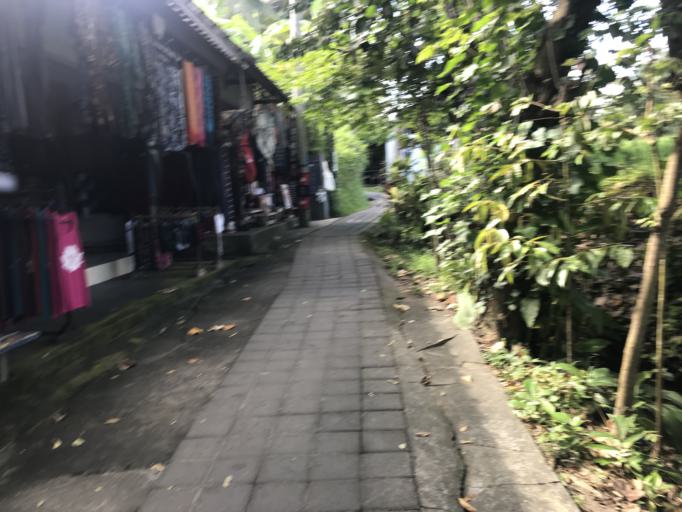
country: ID
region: Bali
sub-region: Kabupaten Gianyar
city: Ubud
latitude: -8.5008
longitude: 115.2584
